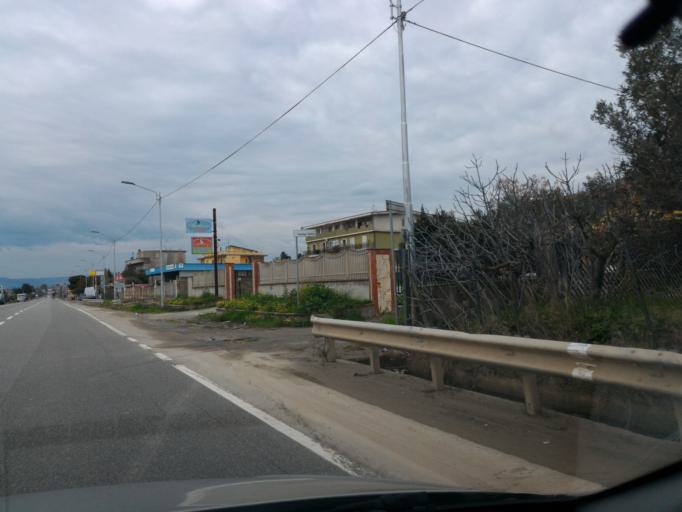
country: IT
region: Calabria
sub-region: Provincia di Catanzaro
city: Barone
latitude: 38.8474
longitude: 16.6589
